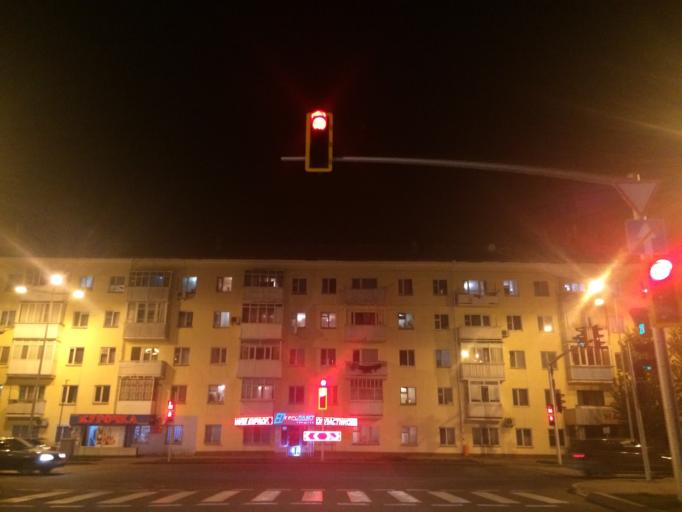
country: KZ
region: Astana Qalasy
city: Astana
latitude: 51.1862
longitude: 71.4190
